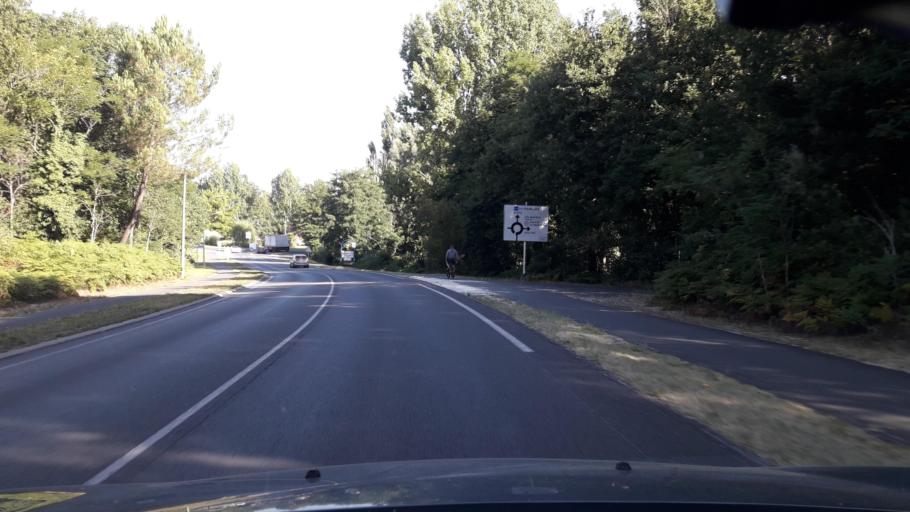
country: FR
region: Poitou-Charentes
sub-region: Departement de la Charente-Maritime
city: Les Mathes
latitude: 45.7108
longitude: -1.1592
